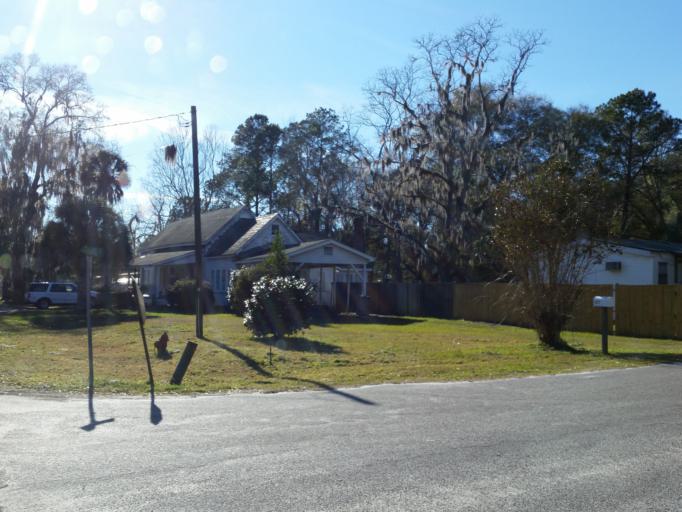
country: US
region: Georgia
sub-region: Echols County
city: Statenville
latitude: 30.6062
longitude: -83.1005
